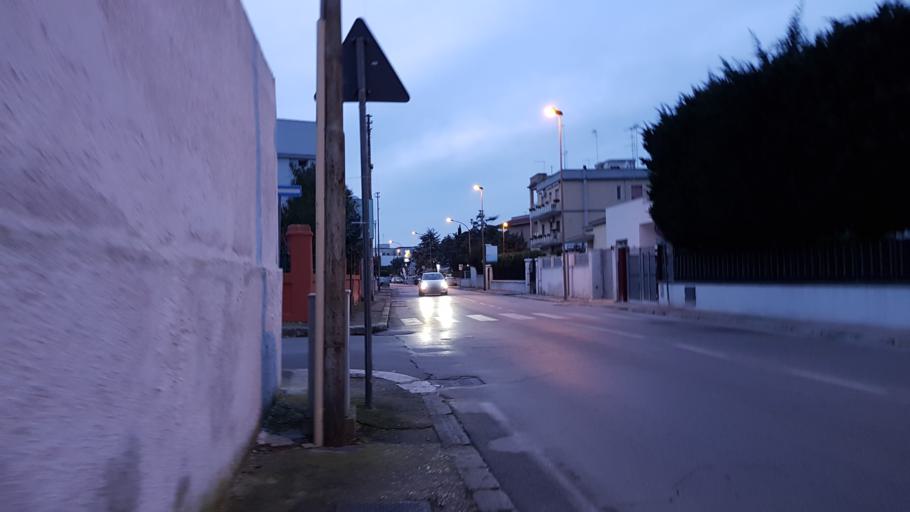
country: IT
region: Apulia
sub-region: Provincia di Brindisi
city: Brindisi
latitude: 40.6485
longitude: 17.9424
